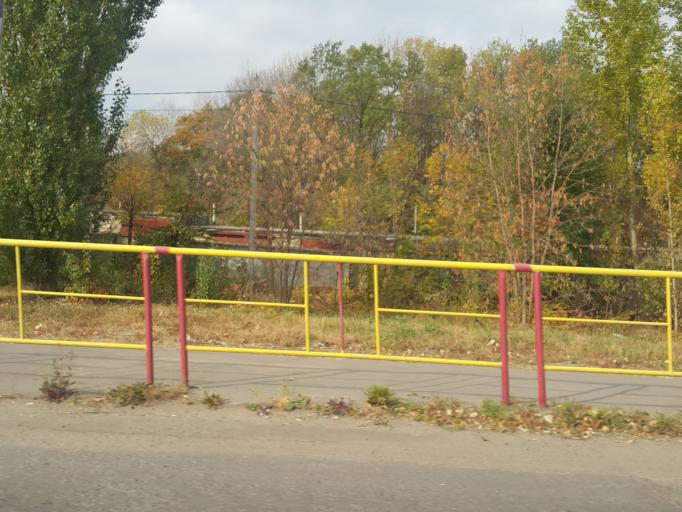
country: RU
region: Tambov
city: Bokino
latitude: 52.6587
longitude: 41.4475
